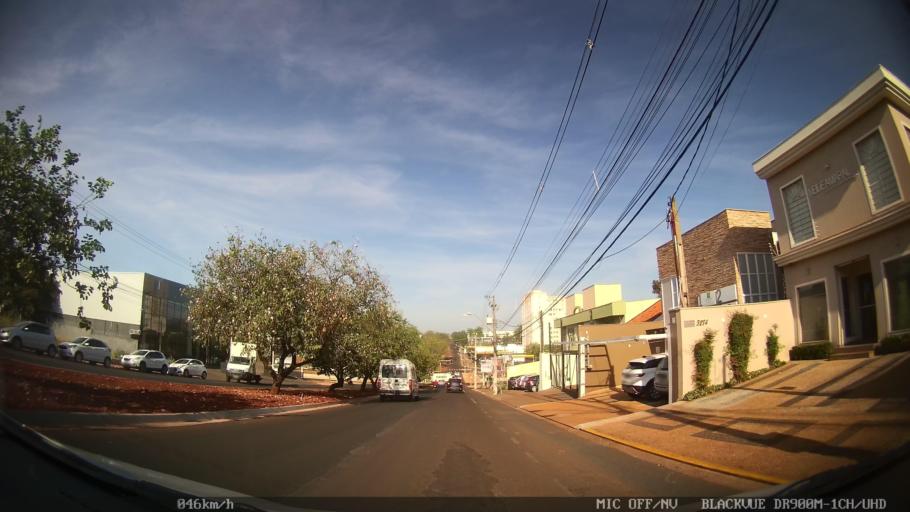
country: BR
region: Sao Paulo
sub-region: Ribeirao Preto
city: Ribeirao Preto
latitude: -21.2027
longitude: -47.8192
